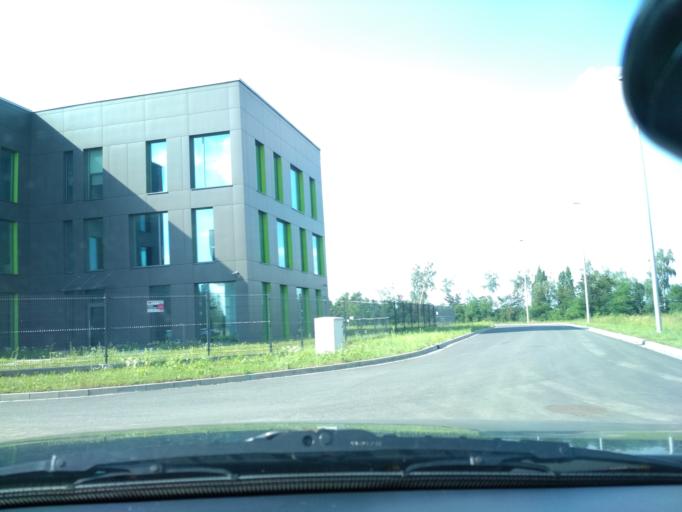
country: PL
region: Silesian Voivodeship
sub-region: Gliwice
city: Gliwice
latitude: 50.2785
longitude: 18.6882
